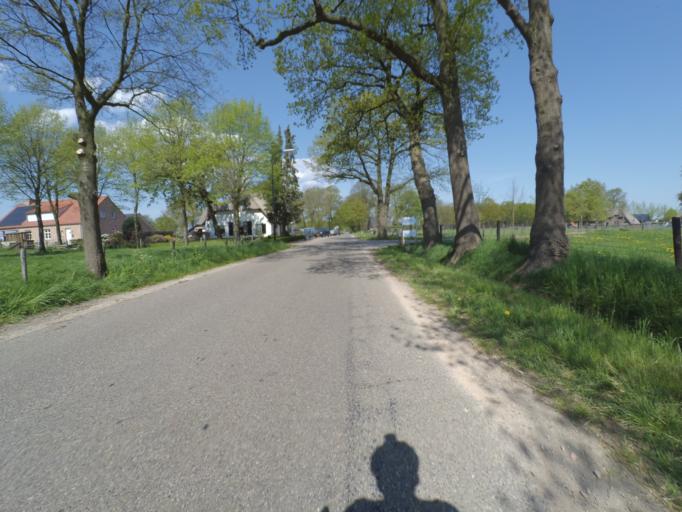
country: NL
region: Gelderland
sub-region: Gemeente Apeldoorn
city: Uddel
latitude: 52.2639
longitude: 5.7713
